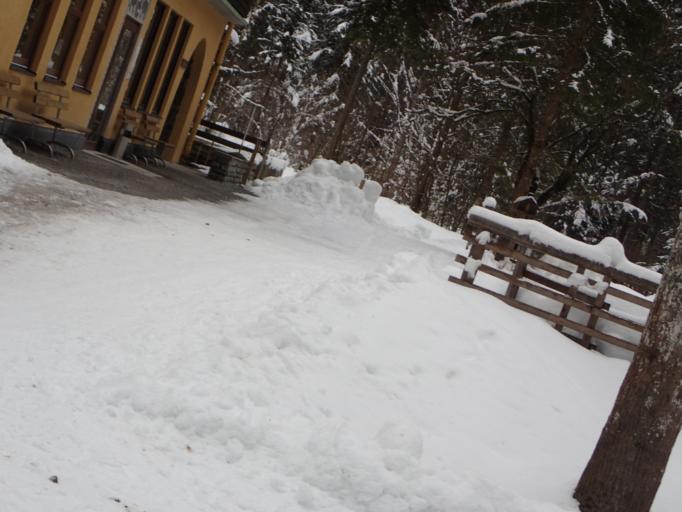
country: AT
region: Salzburg
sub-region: Politischer Bezirk Hallein
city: Golling an der Salzach
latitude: 47.5714
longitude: 13.1247
